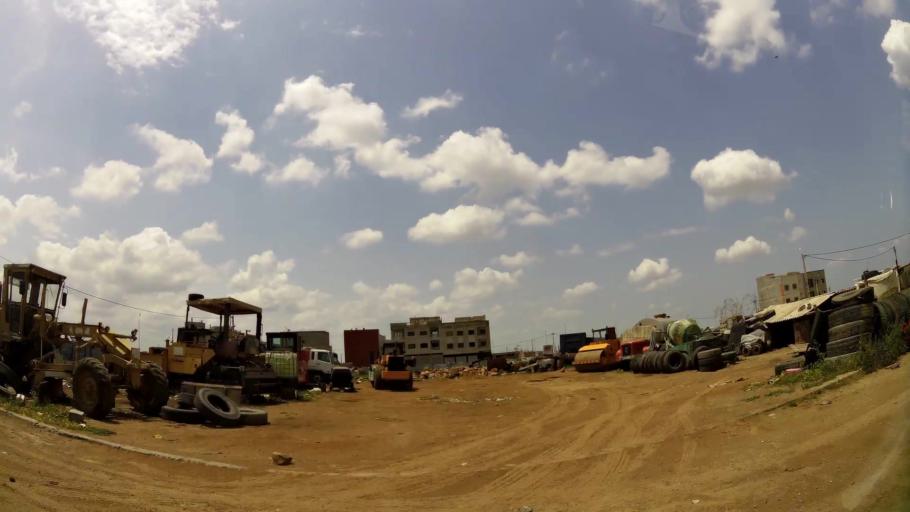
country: MA
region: Rabat-Sale-Zemmour-Zaer
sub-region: Khemisset
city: Tiflet
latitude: 34.0057
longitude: -6.5366
